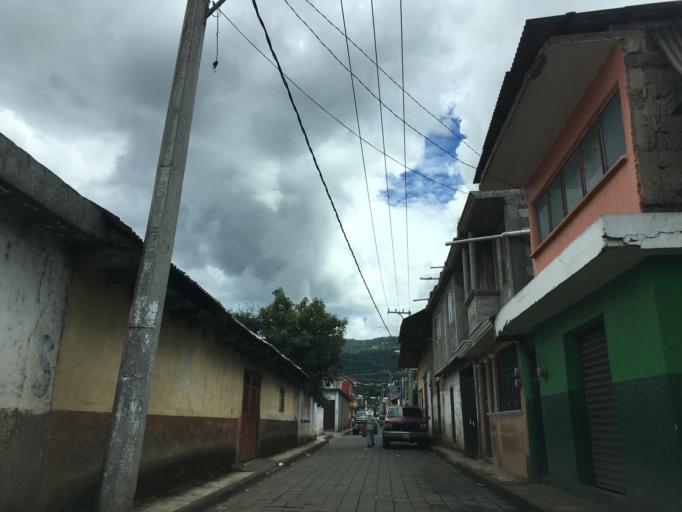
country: MX
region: Michoacan
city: Nahuatzen
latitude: 19.6536
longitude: -101.9182
